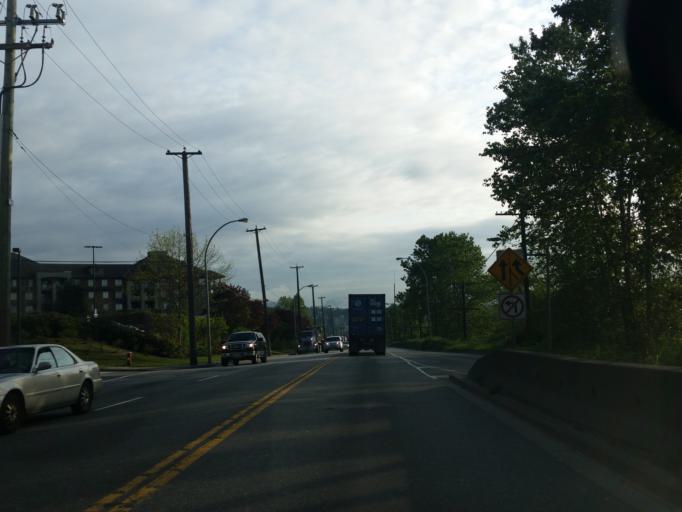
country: CA
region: British Columbia
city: New Westminster
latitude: 49.2250
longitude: -122.8897
